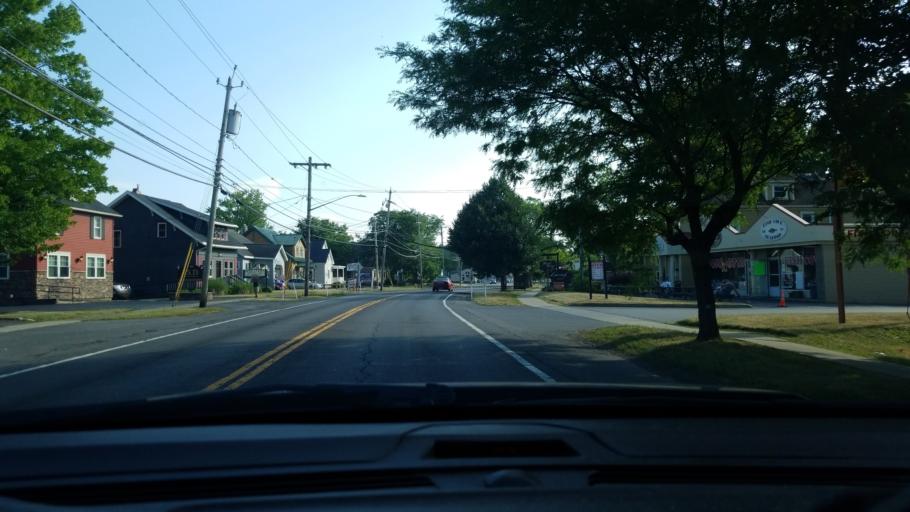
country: US
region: New York
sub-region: Onondaga County
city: North Syracuse
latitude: 43.1277
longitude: -76.1356
